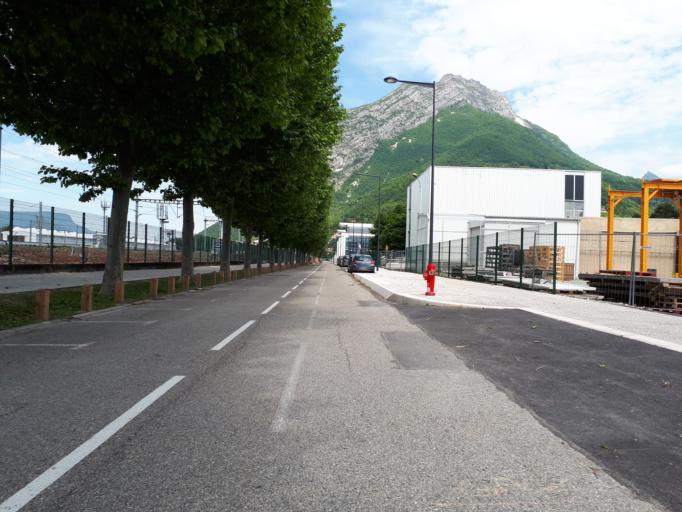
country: FR
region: Rhone-Alpes
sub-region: Departement de l'Isere
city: Saint-Martin-le-Vinoux
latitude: 45.2009
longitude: 5.7101
